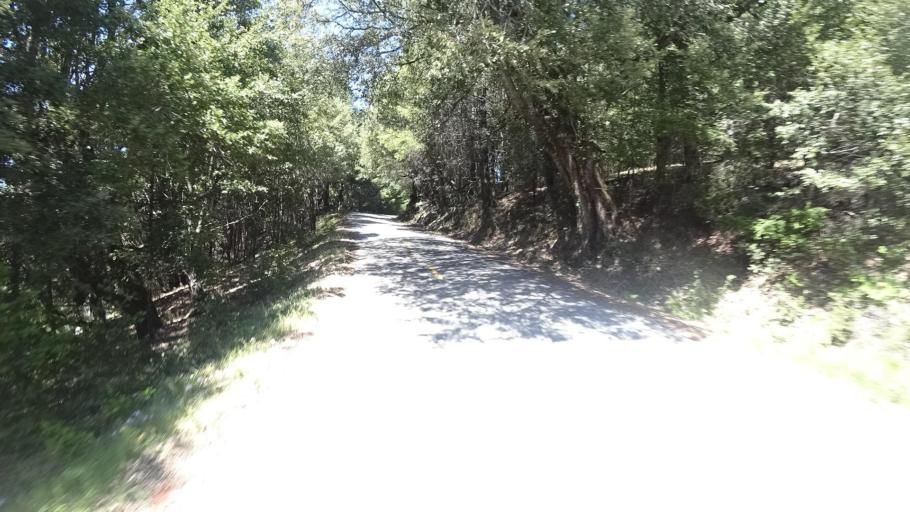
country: US
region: California
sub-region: Humboldt County
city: Rio Dell
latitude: 40.2529
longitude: -124.1179
